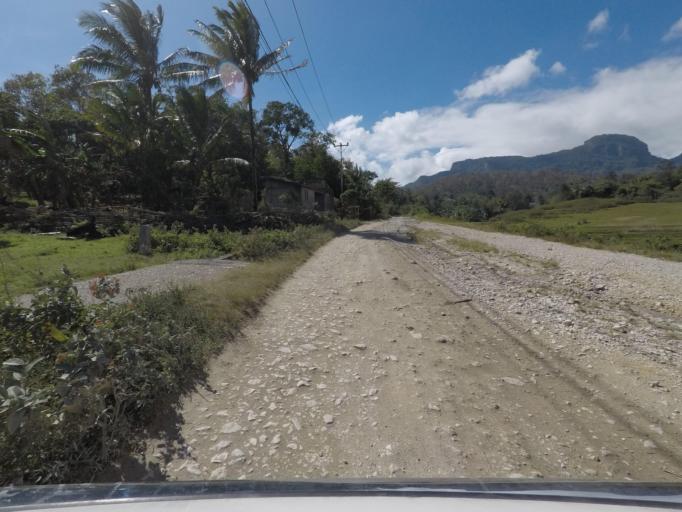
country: TL
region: Baucau
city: Venilale
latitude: -8.6736
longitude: 126.3673
